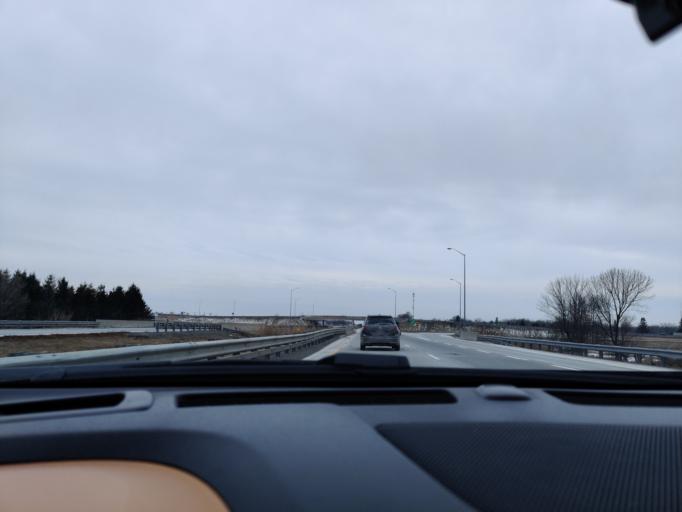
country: US
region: New York
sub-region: St. Lawrence County
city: Massena
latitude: 45.0127
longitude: -74.9937
